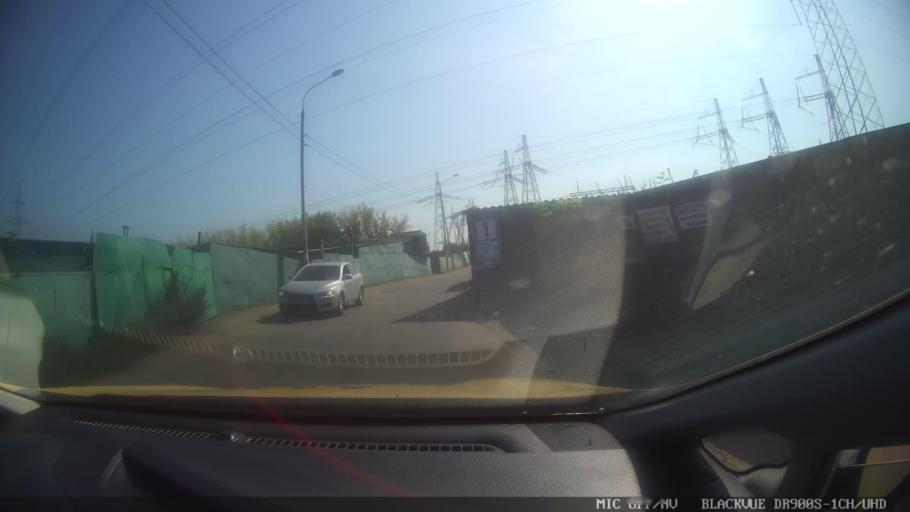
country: RU
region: Moscow
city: Bibirevo
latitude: 55.8803
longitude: 37.6013
